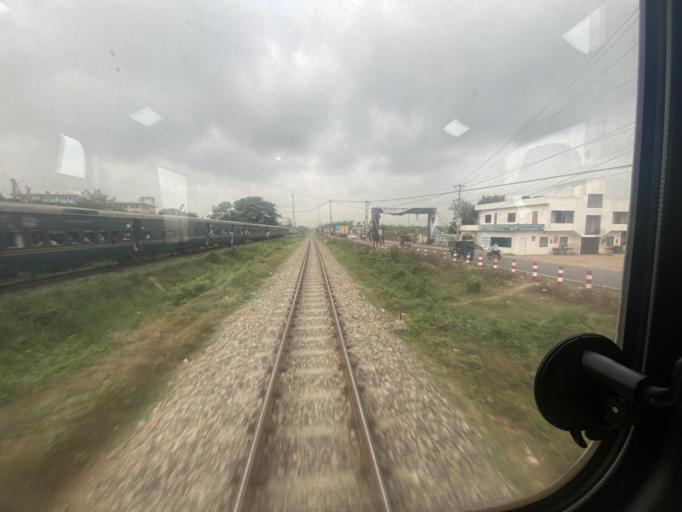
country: BD
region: Dhaka
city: Tungi
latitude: 23.9141
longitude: 90.4233
